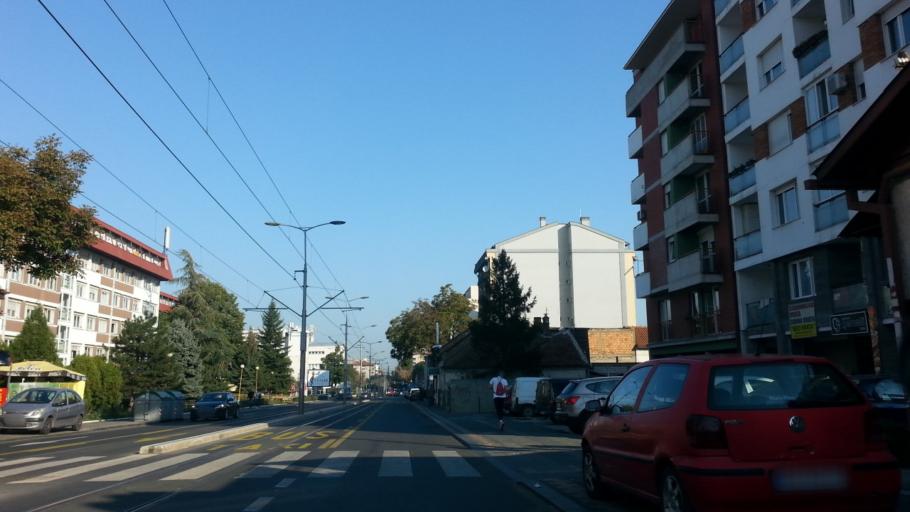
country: RS
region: Central Serbia
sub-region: Belgrade
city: Vozdovac
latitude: 44.7627
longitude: 20.4838
